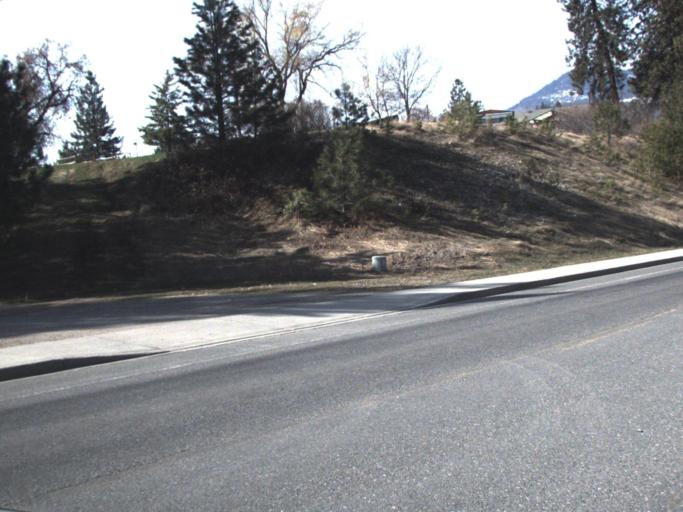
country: US
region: Washington
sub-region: Stevens County
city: Colville
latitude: 48.5470
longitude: -117.8838
